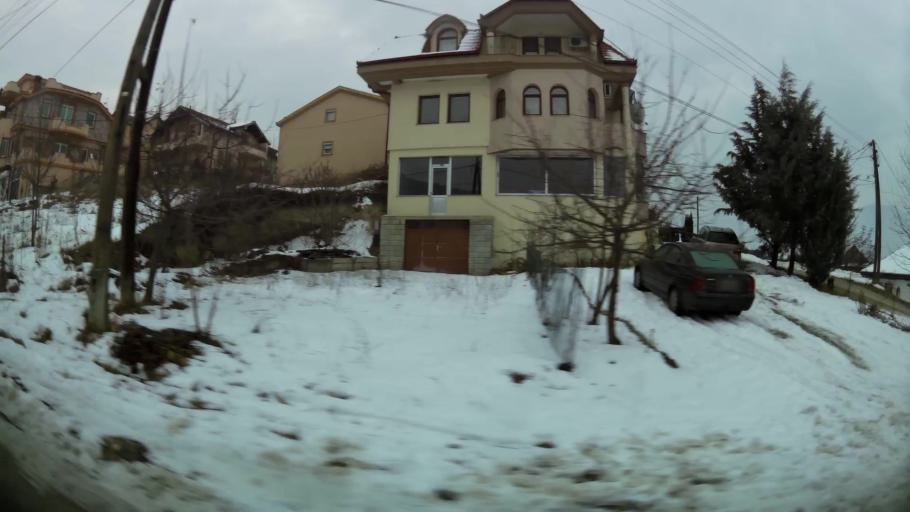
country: MK
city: Kondovo
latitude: 42.0134
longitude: 21.3064
